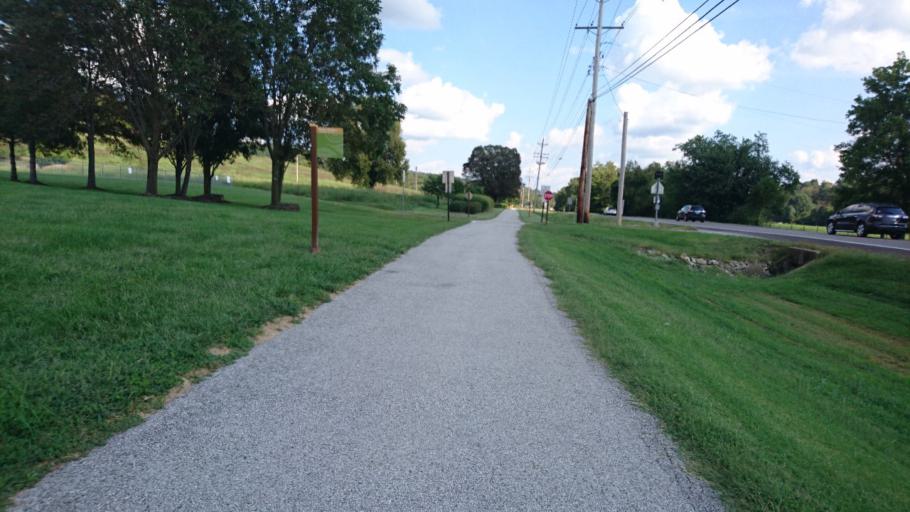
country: US
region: Missouri
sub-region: Saint Louis County
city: Wildwood
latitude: 38.5501
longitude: -90.6371
